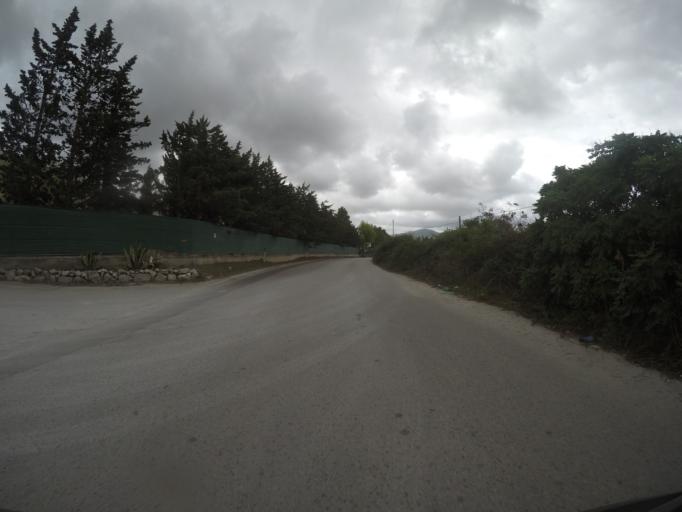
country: IT
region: Sicily
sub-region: Palermo
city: Montelepre
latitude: 38.1050
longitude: 13.1709
